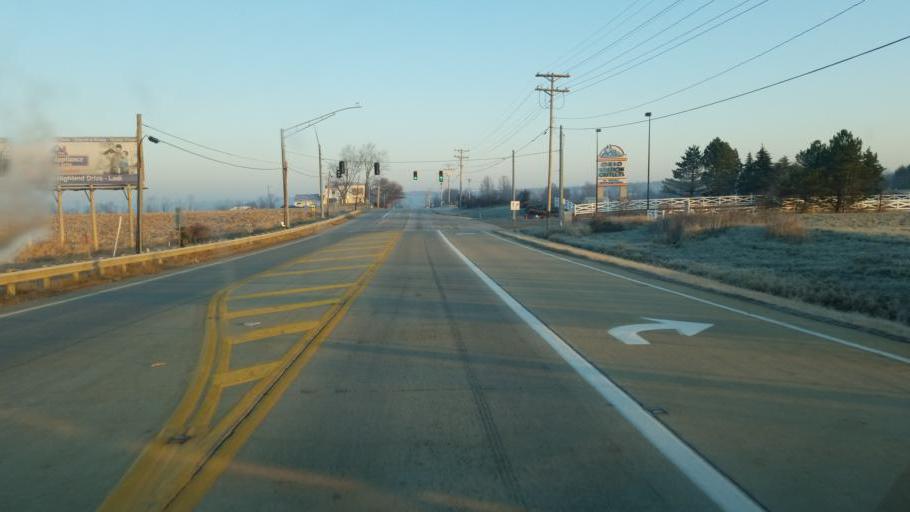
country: US
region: Ohio
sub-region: Medina County
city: Lodi
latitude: 41.0028
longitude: -81.9962
